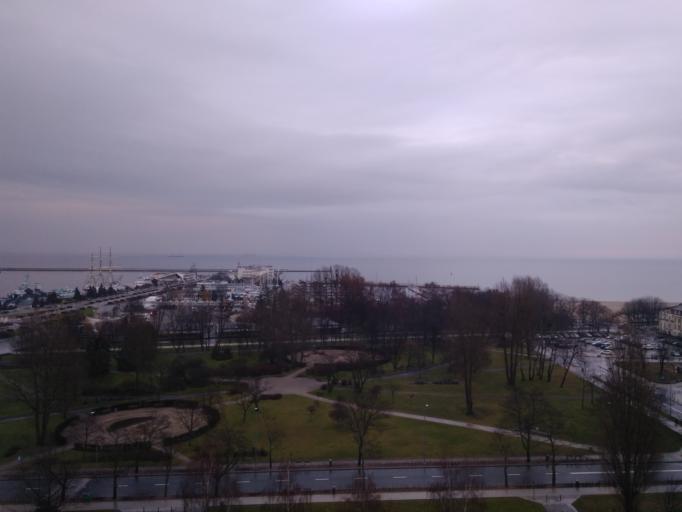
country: PL
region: Pomeranian Voivodeship
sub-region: Gdynia
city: Gdynia
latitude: 54.5178
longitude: 18.5446
